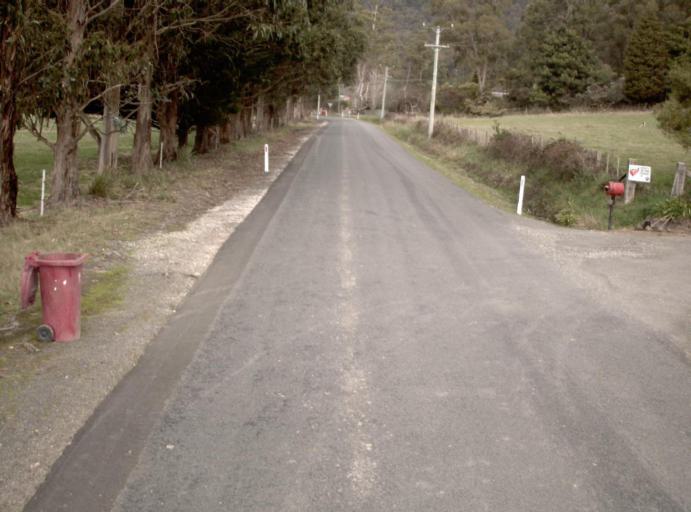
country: AU
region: Tasmania
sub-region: Launceston
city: Mayfield
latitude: -41.2669
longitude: 147.1607
